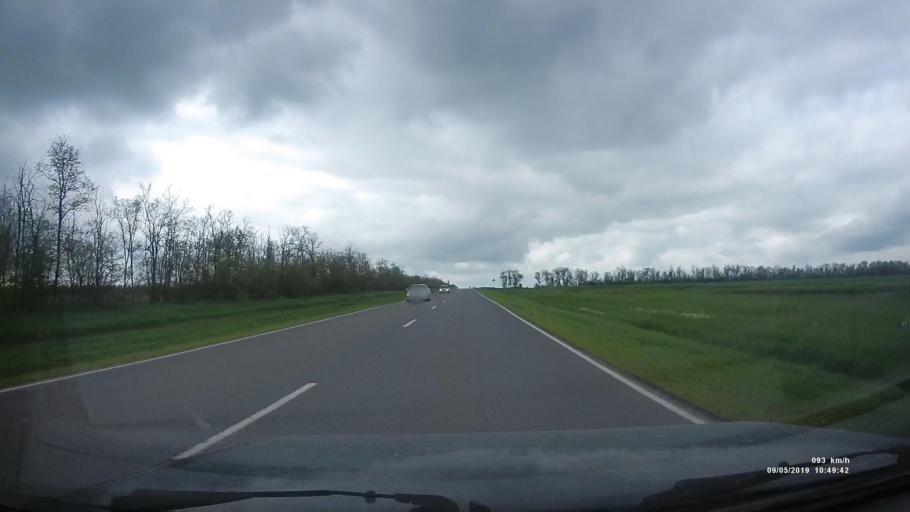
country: RU
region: Rostov
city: Peshkovo
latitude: 46.9387
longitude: 39.3554
